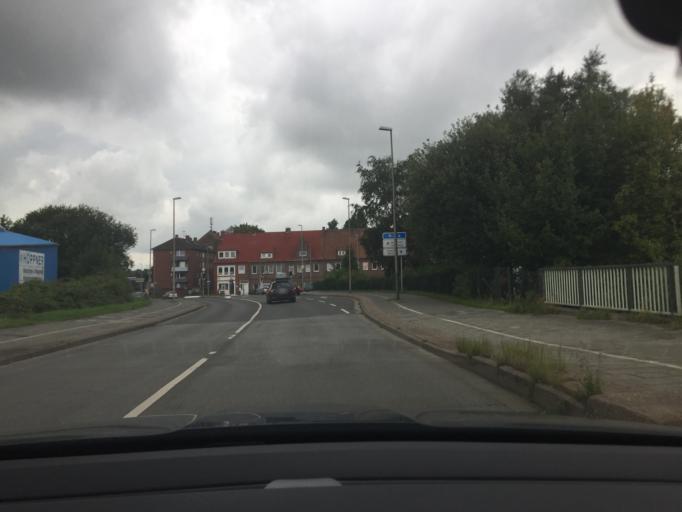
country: DE
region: Lower Saxony
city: Emden
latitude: 53.3607
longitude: 7.2038
